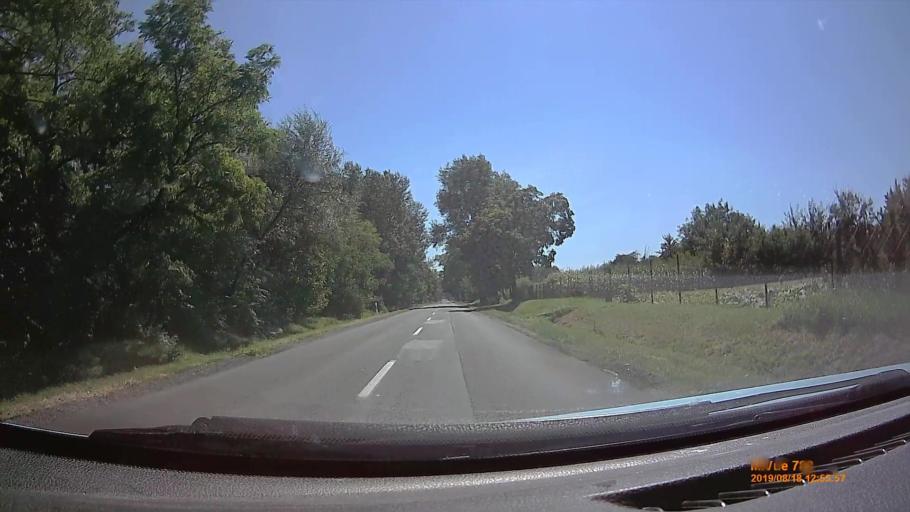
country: HU
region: Fejer
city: Aba
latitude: 47.0294
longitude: 18.5389
